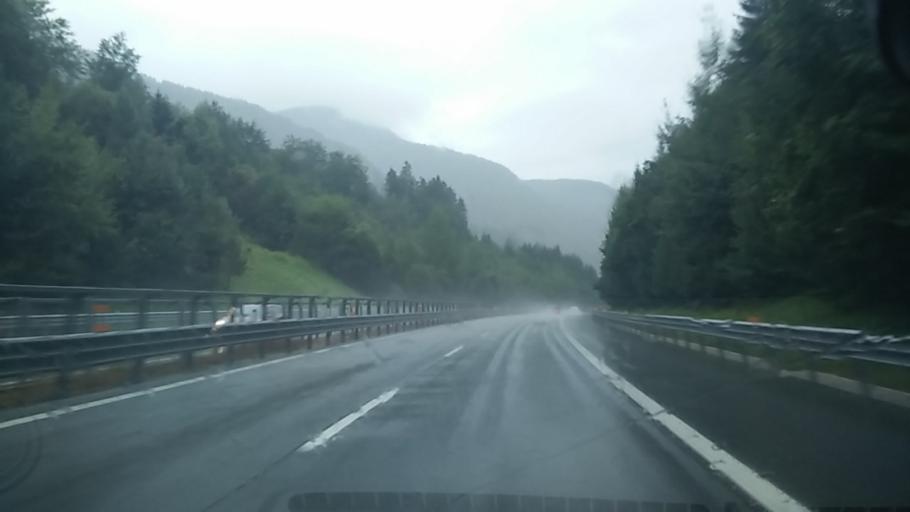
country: IT
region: Friuli Venezia Giulia
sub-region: Provincia di Udine
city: Malborghetto
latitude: 46.4979
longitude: 13.3995
